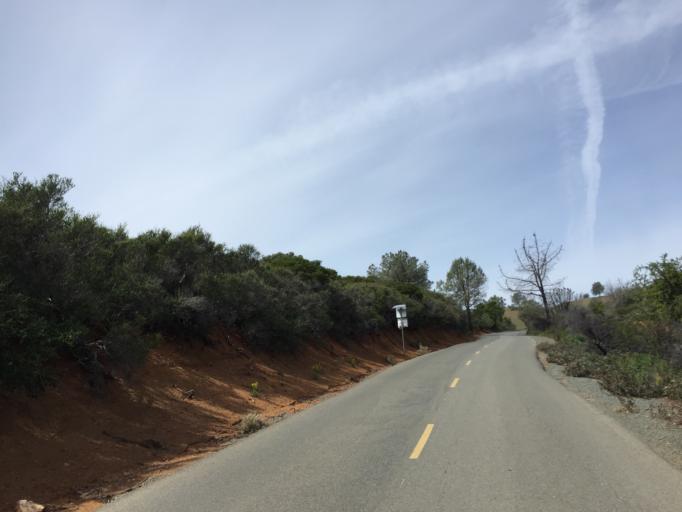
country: US
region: California
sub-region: Contra Costa County
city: Diablo
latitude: 37.8661
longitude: -121.9233
